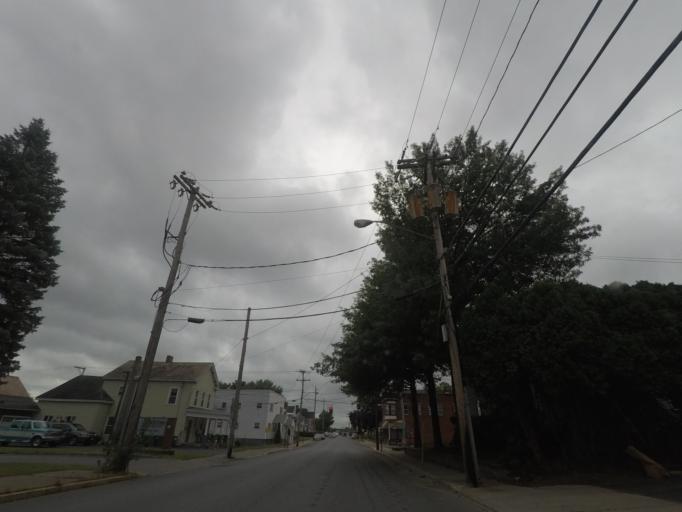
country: US
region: New York
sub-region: Saratoga County
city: Mechanicville
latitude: 42.9083
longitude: -73.6838
